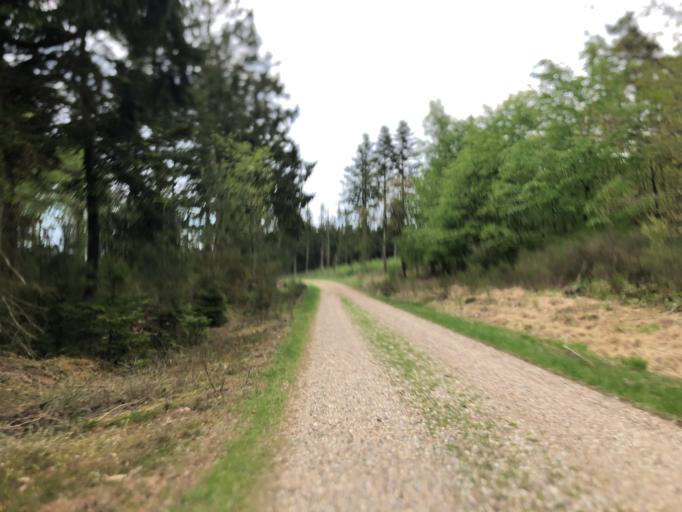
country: DK
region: Central Jutland
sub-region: Holstebro Kommune
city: Ulfborg
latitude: 56.2840
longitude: 8.4337
